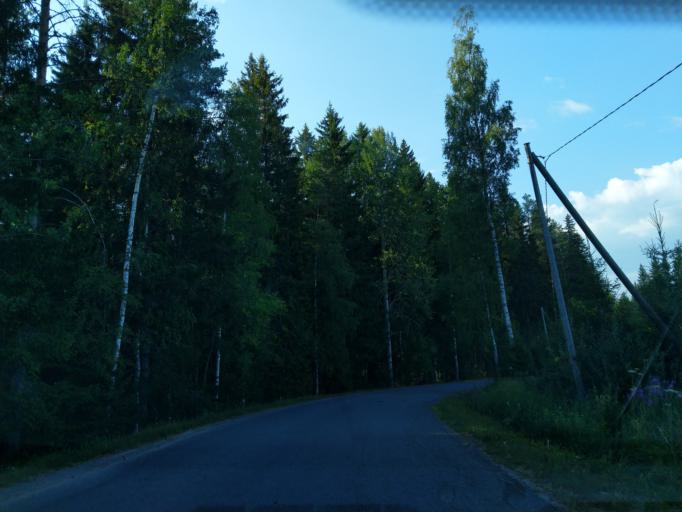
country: FI
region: Satakunta
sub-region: Pori
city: Laengelmaeki
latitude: 61.8099
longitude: 22.1892
